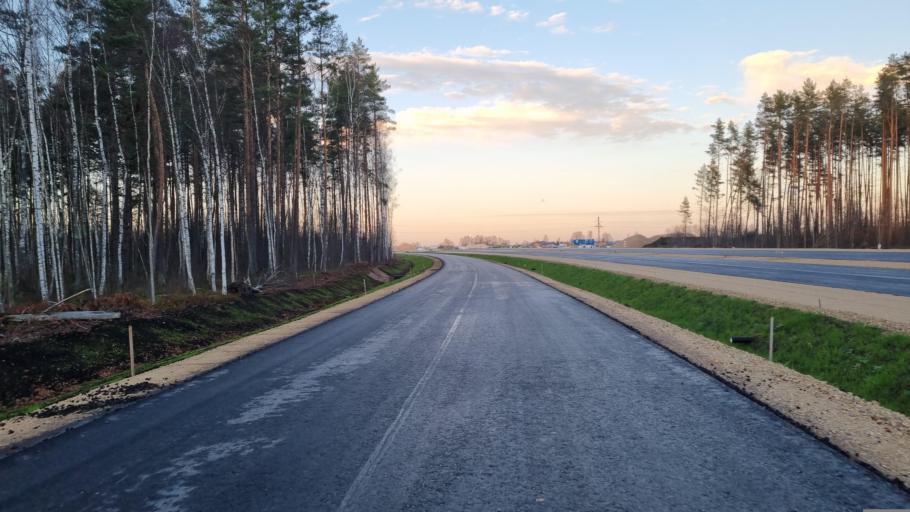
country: LV
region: Kekava
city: Balozi
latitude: 56.8685
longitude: 24.1661
